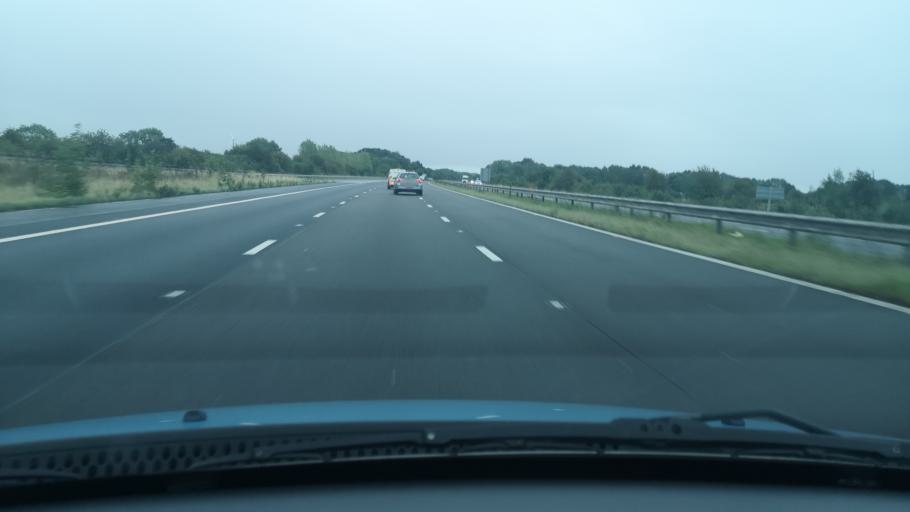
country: GB
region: England
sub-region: North Lincolnshire
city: Belton
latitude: 53.5689
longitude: -0.8153
